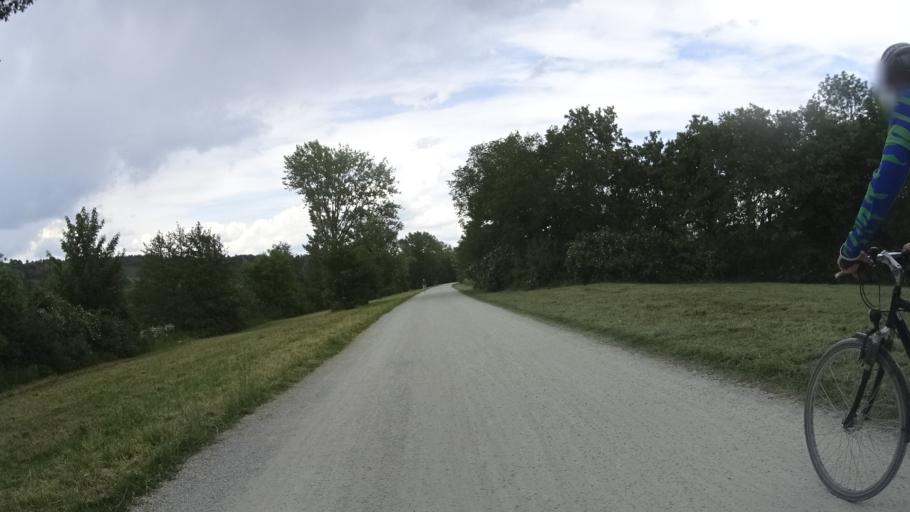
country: DE
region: Bavaria
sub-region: Upper Palatinate
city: Sinzing
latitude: 49.0251
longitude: 12.0473
